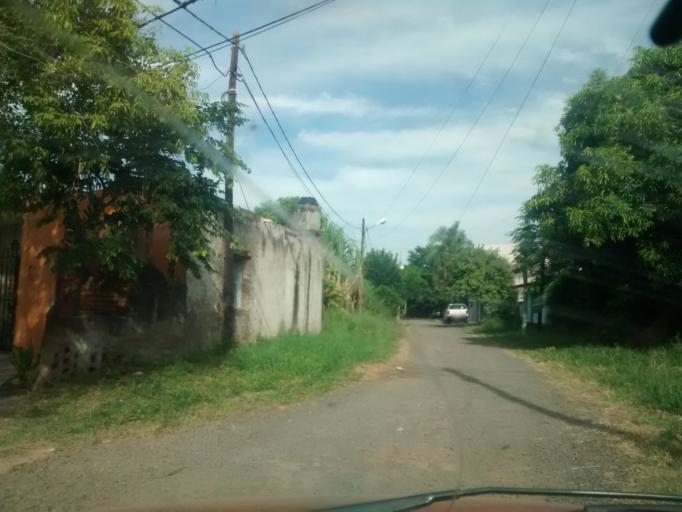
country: AR
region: Chaco
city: Resistencia
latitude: -27.4377
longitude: -58.9967
